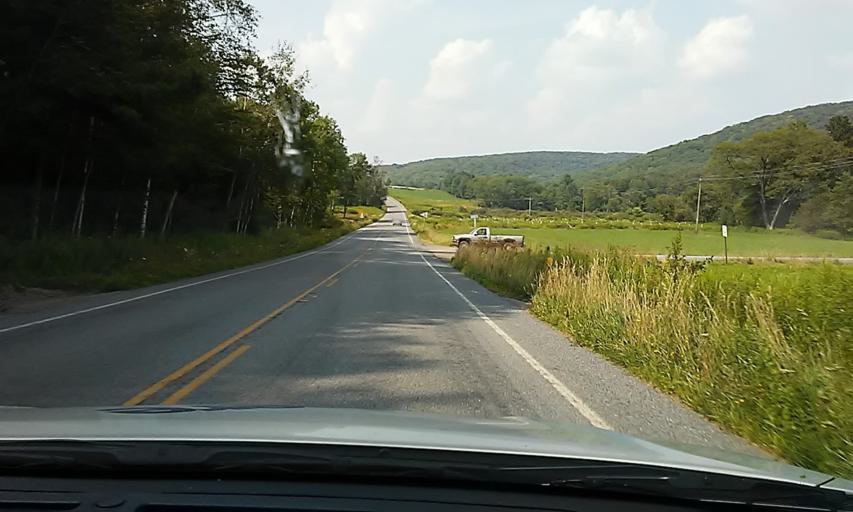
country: US
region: Pennsylvania
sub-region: Potter County
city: Coudersport
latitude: 41.9032
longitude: -77.8424
